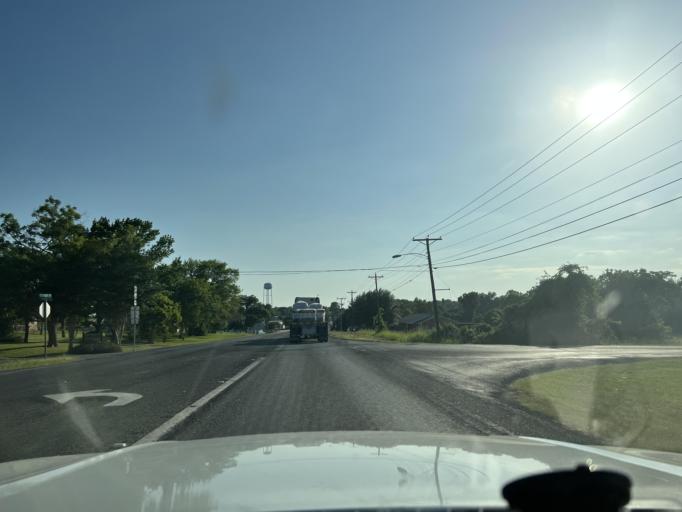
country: US
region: Texas
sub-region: Washington County
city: Brenham
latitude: 30.1779
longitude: -96.3929
